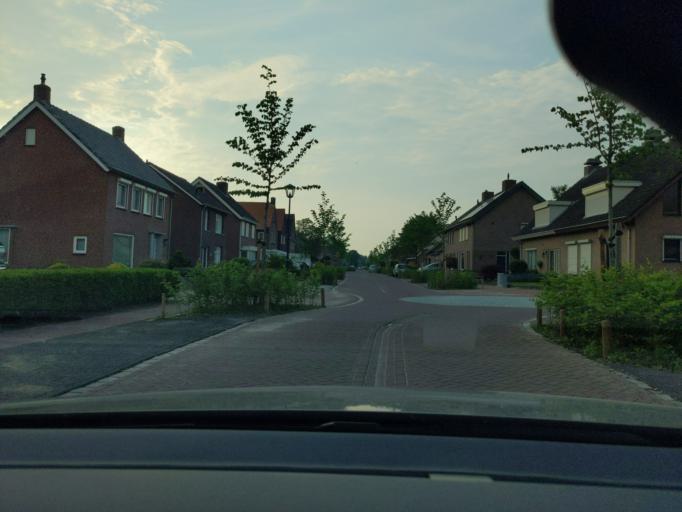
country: NL
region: North Brabant
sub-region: Gemeente Bladel en Netersel
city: Bladel
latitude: 51.3570
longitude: 5.1683
